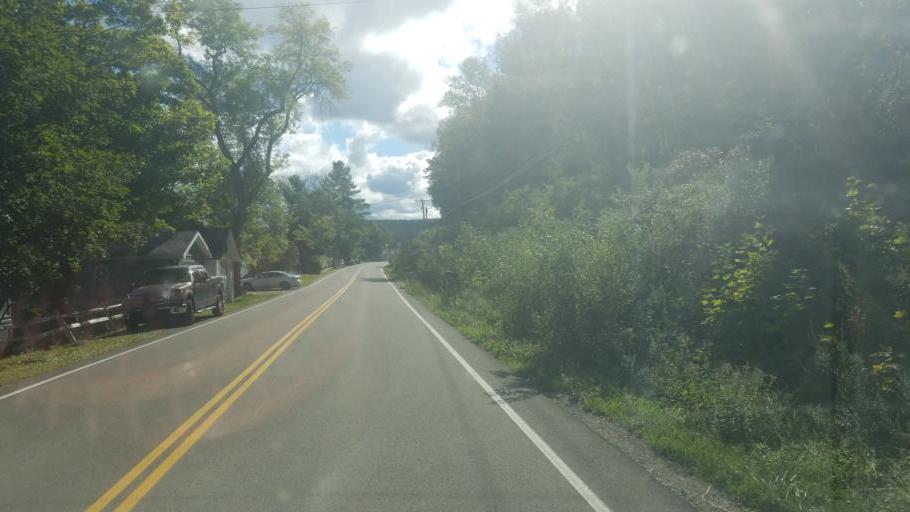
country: US
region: New York
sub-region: Allegany County
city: Cuba
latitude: 42.2481
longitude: -78.2833
